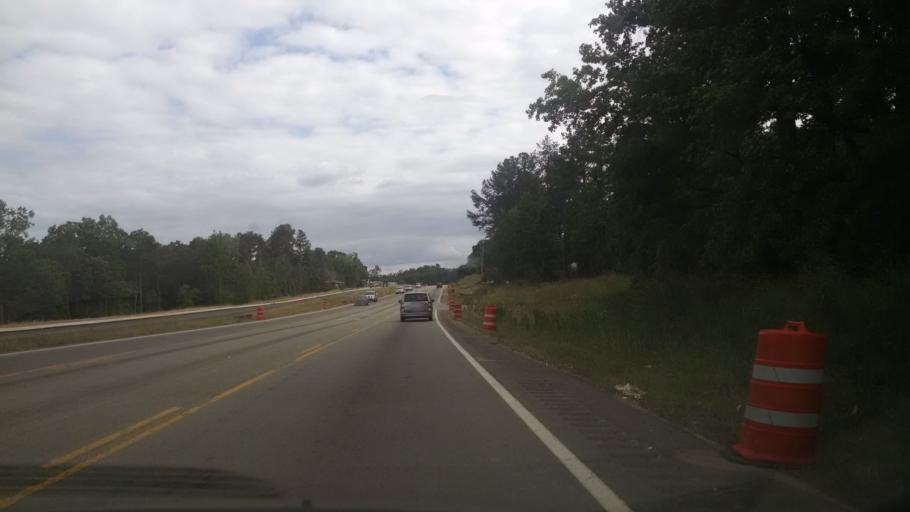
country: US
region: Georgia
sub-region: Forsyth County
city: Cumming
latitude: 34.1479
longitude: -84.1048
